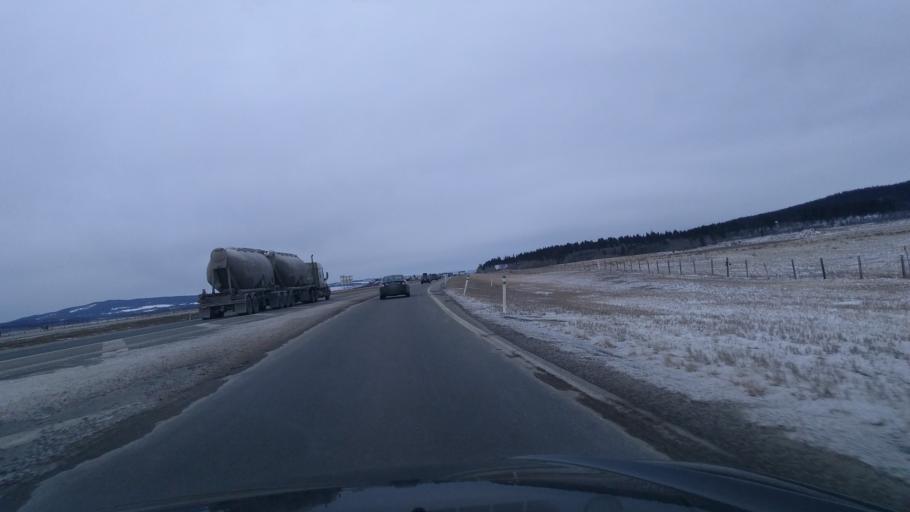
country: CA
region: Alberta
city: Canmore
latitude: 51.1054
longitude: -115.0157
